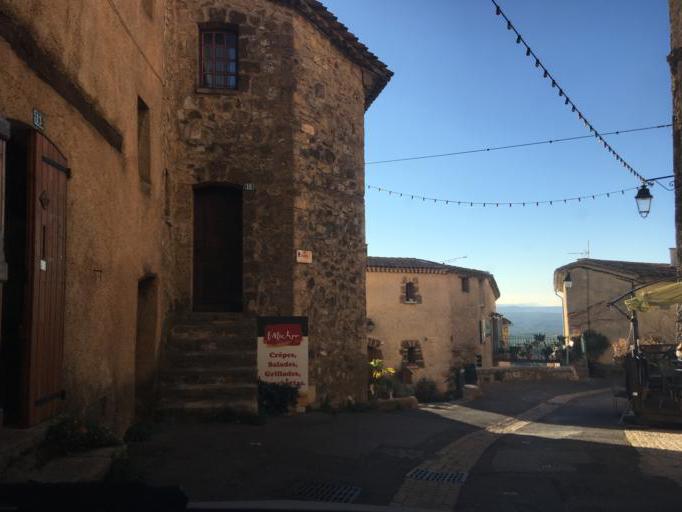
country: FR
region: Provence-Alpes-Cote d'Azur
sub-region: Departement du Var
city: Villecroze
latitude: 43.5891
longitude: 6.3019
